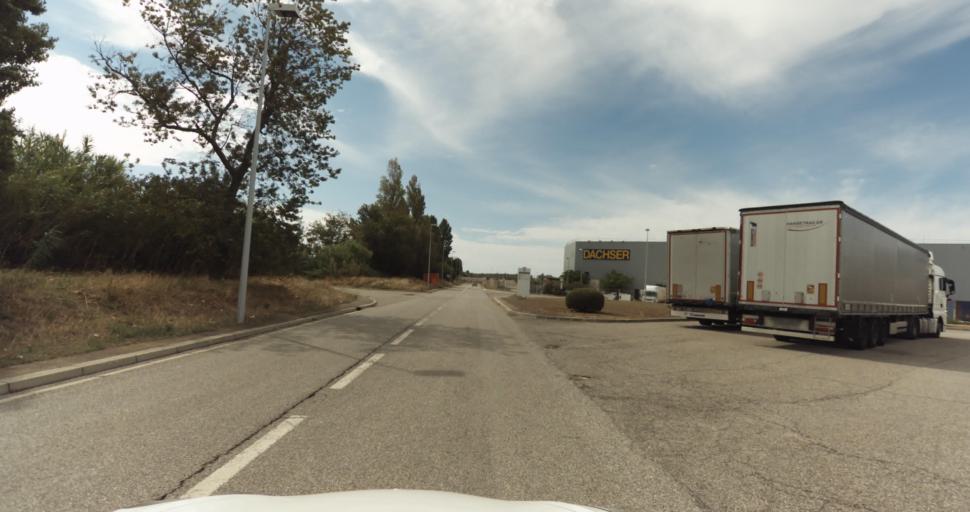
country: FR
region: Provence-Alpes-Cote d'Azur
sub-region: Departement des Bouches-du-Rhone
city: Miramas
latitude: 43.6038
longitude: 4.9993
